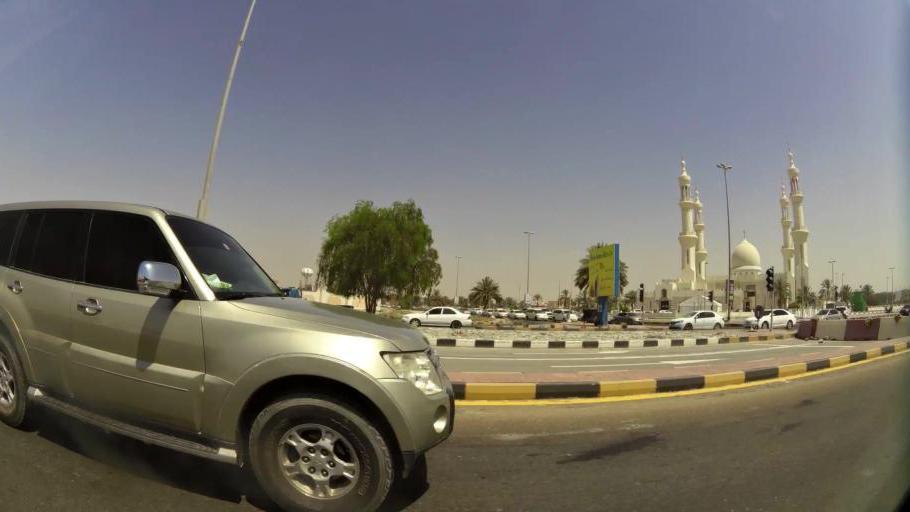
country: AE
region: Ajman
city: Ajman
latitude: 25.4187
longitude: 55.4887
